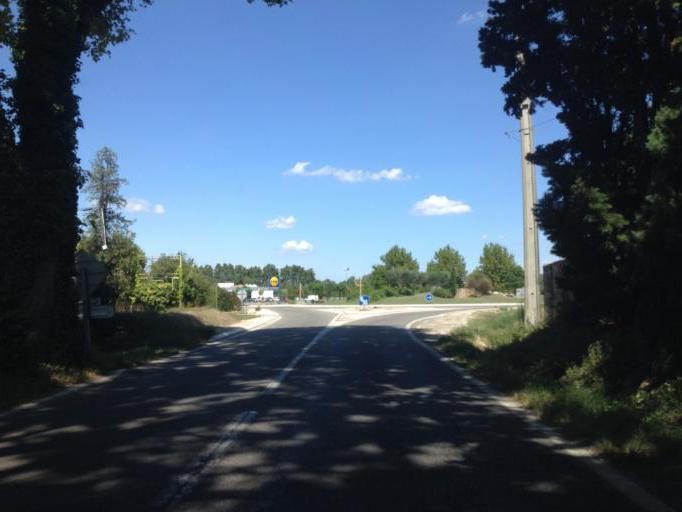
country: FR
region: Languedoc-Roussillon
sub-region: Departement du Gard
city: Roquemaure
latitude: 44.0428
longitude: 4.7887
